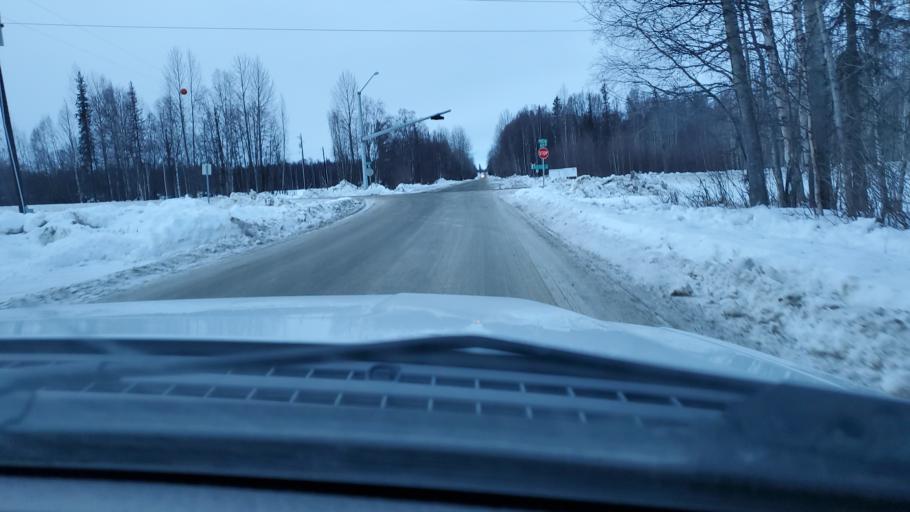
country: US
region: Alaska
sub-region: Matanuska-Susitna Borough
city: Y
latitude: 62.3163
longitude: -150.2326
